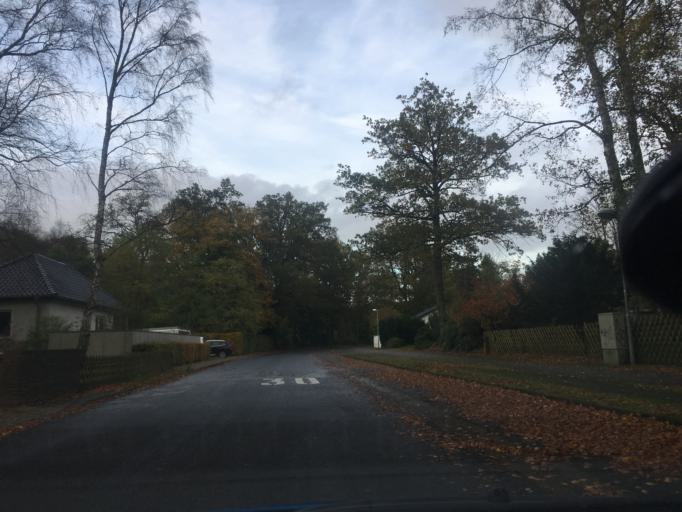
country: DE
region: Lower Saxony
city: Lueneburg
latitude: 53.2330
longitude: 10.4167
